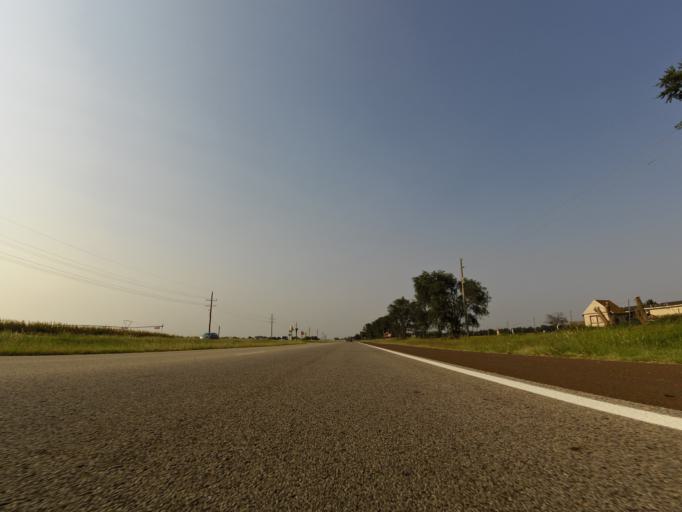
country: US
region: Kansas
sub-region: Reno County
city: South Hutchinson
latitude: 37.9866
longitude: -97.9401
